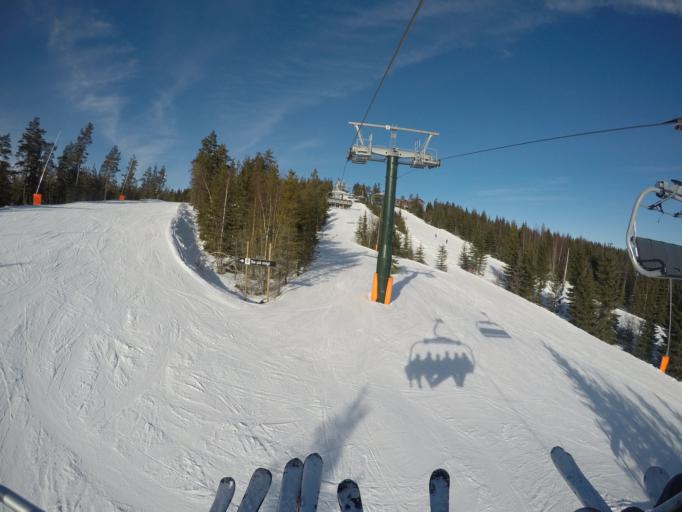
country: SE
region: Dalarna
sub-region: Borlange Kommun
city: Borlaenge
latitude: 60.3809
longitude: 15.4023
